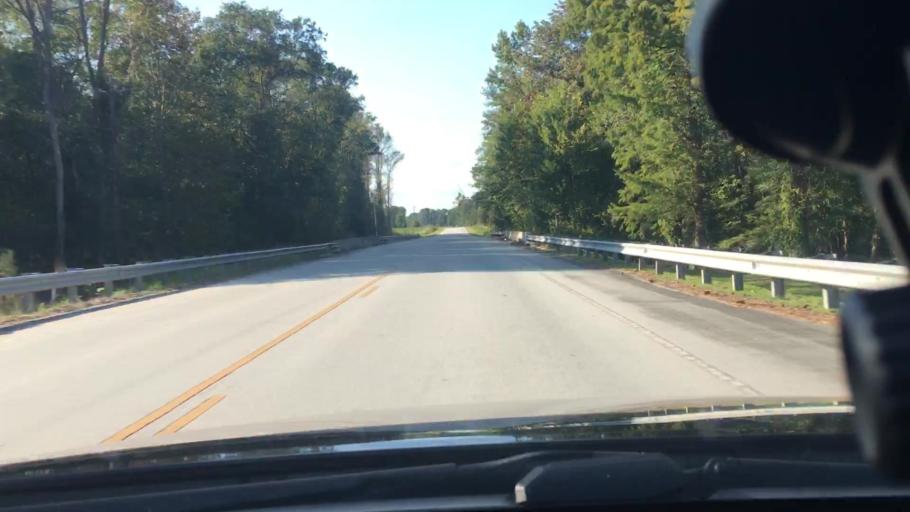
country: US
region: North Carolina
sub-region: Craven County
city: Vanceboro
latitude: 35.3365
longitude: -77.1739
